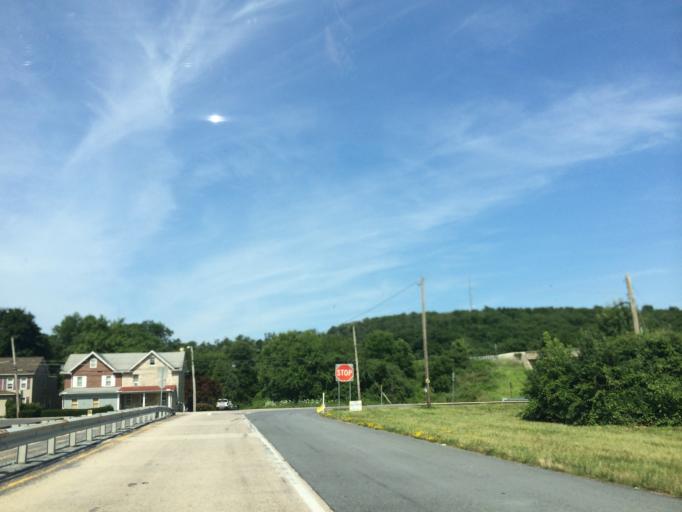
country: US
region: Pennsylvania
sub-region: Berks County
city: Kutztown
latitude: 40.5259
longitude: -75.7809
